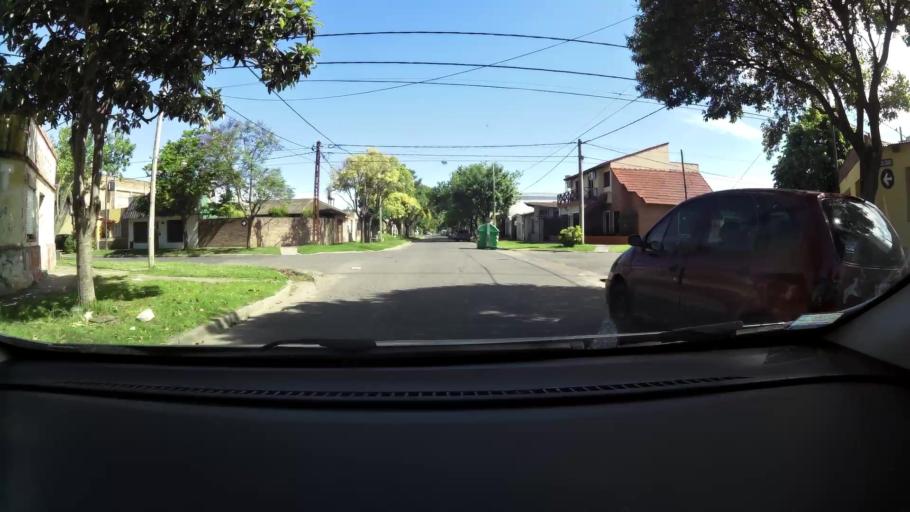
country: AR
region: Santa Fe
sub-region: Departamento de Rosario
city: Rosario
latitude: -32.9357
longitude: -60.7163
